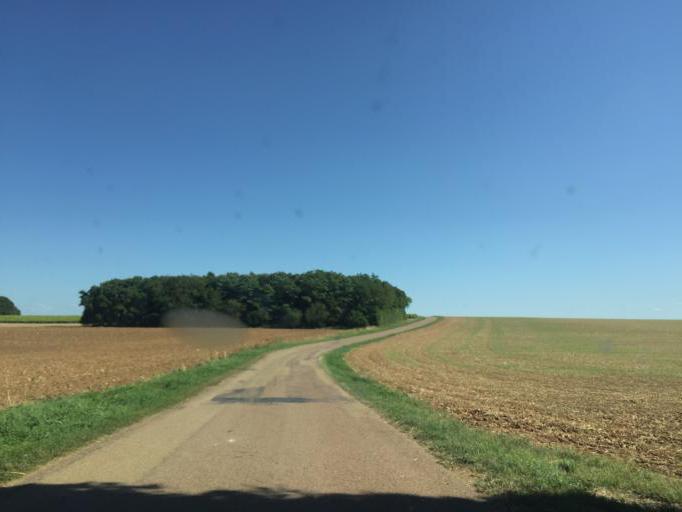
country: FR
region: Bourgogne
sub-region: Departement de l'Yonne
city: Fontenailles
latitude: 47.5359
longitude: 3.3414
